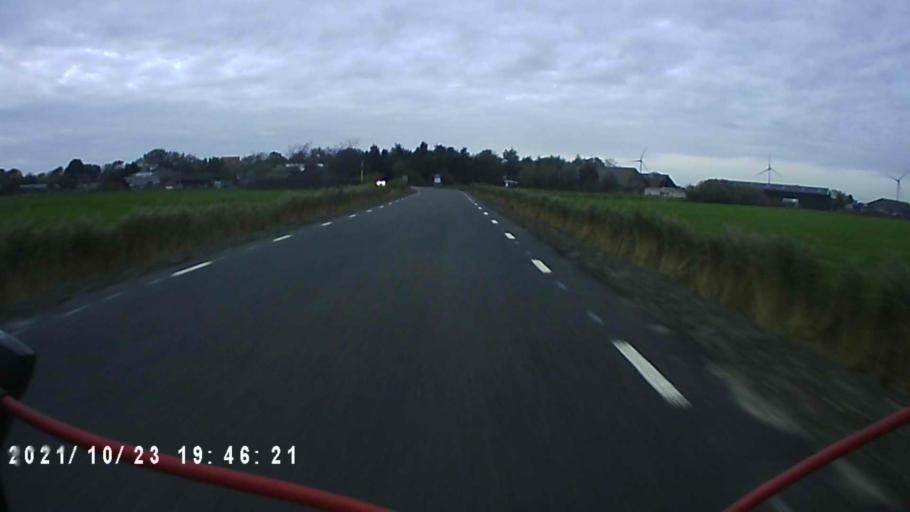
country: NL
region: Friesland
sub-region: Sudwest Fryslan
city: Makkum
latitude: 53.0813
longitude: 5.4264
